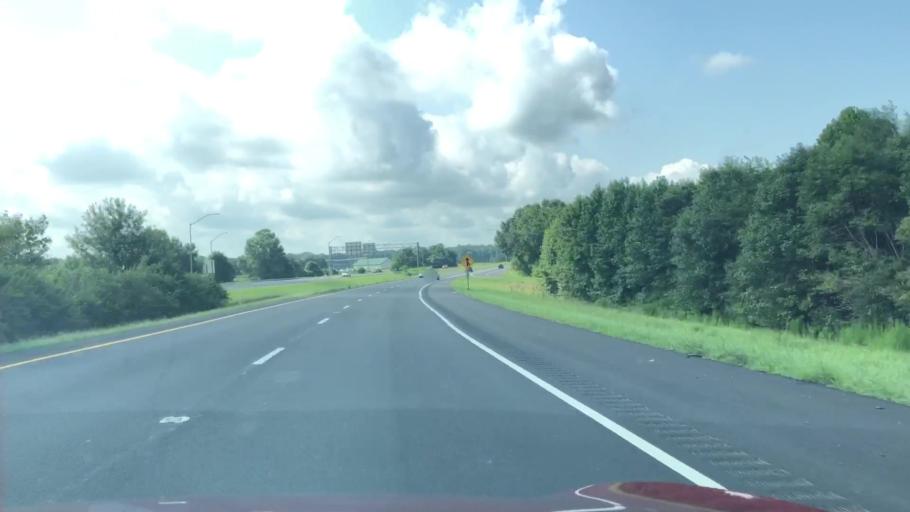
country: US
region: Maryland
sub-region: Wicomico County
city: Salisbury
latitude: 38.3669
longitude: -75.5346
